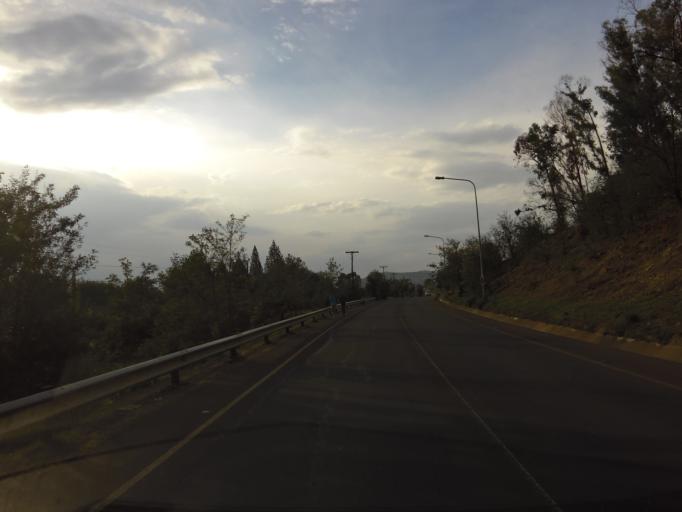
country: LS
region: Maseru
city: Maseru
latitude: -29.3169
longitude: 27.4720
